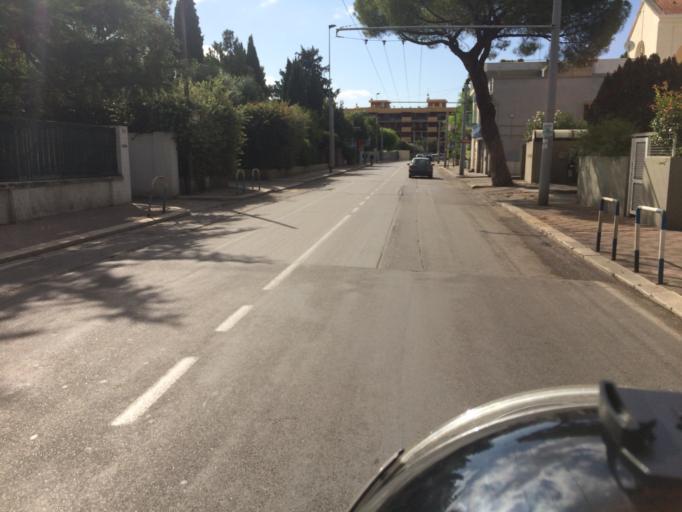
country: IT
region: Apulia
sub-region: Provincia di Bari
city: Bari
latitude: 41.0798
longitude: 16.8698
